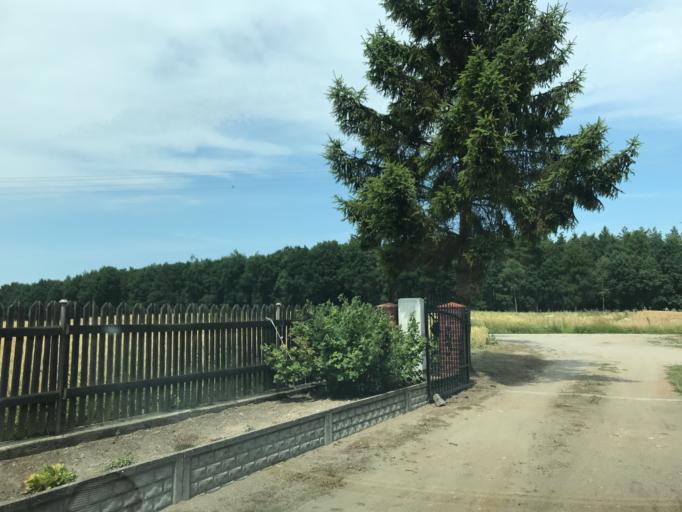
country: PL
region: Kujawsko-Pomorskie
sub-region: Powiat brodnicki
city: Bartniczka
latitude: 53.2585
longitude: 19.5706
